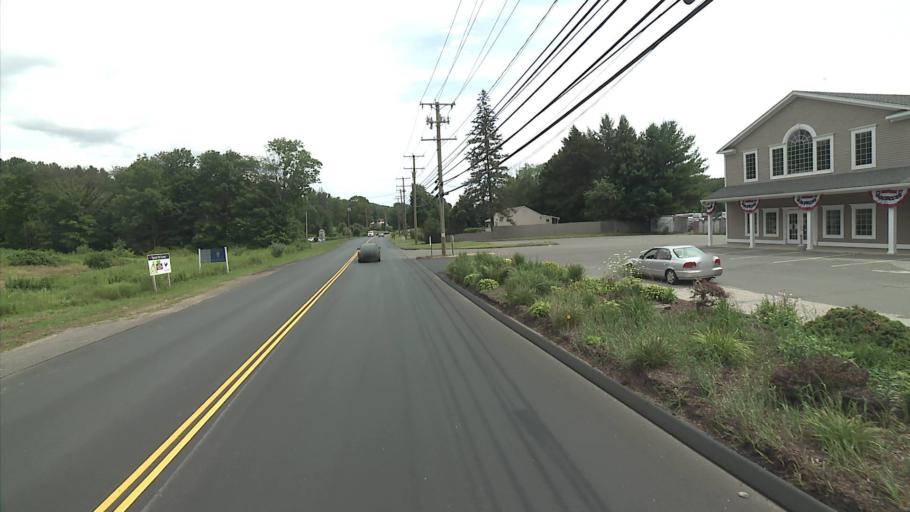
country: US
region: Connecticut
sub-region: New Haven County
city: Seymour
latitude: 41.4087
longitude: -73.0956
